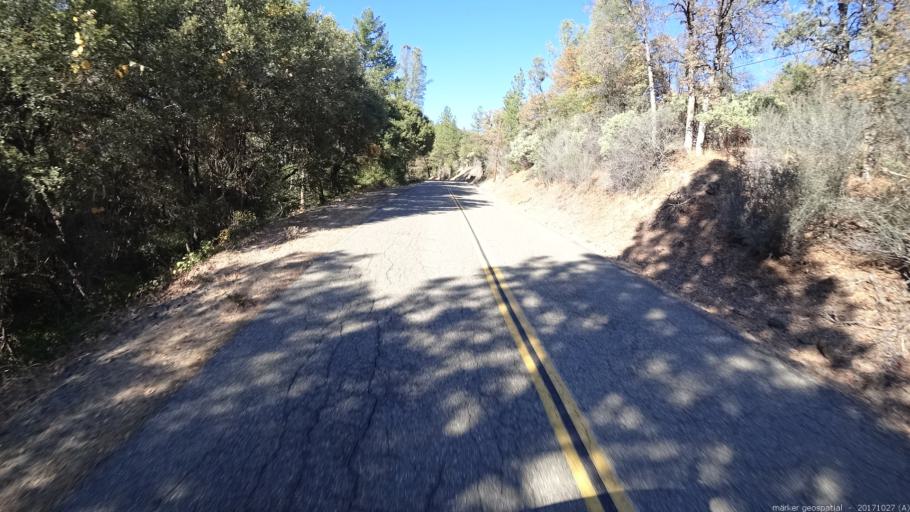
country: US
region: California
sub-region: Shasta County
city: Shingletown
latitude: 40.6827
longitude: -121.8809
